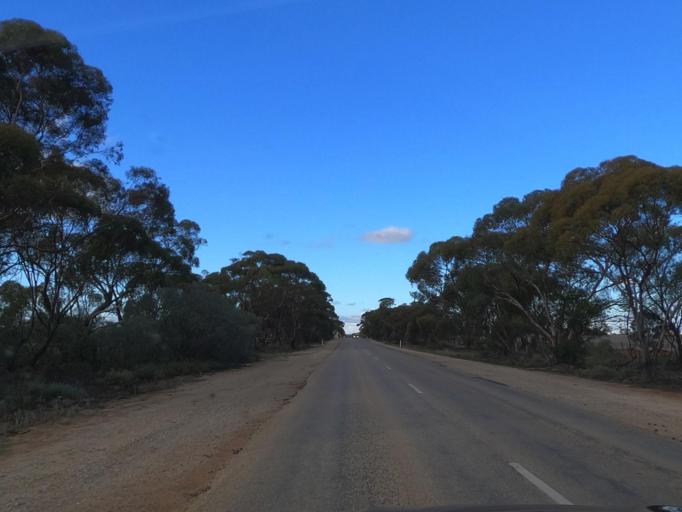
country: AU
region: Victoria
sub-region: Swan Hill
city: Swan Hill
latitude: -35.3471
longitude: 143.5193
